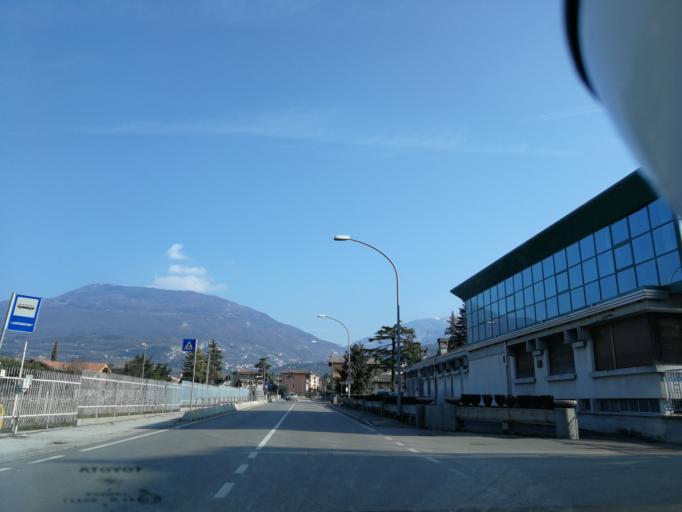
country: IT
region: Trentino-Alto Adige
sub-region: Provincia di Trento
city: Isera
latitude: 45.8883
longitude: 11.0189
